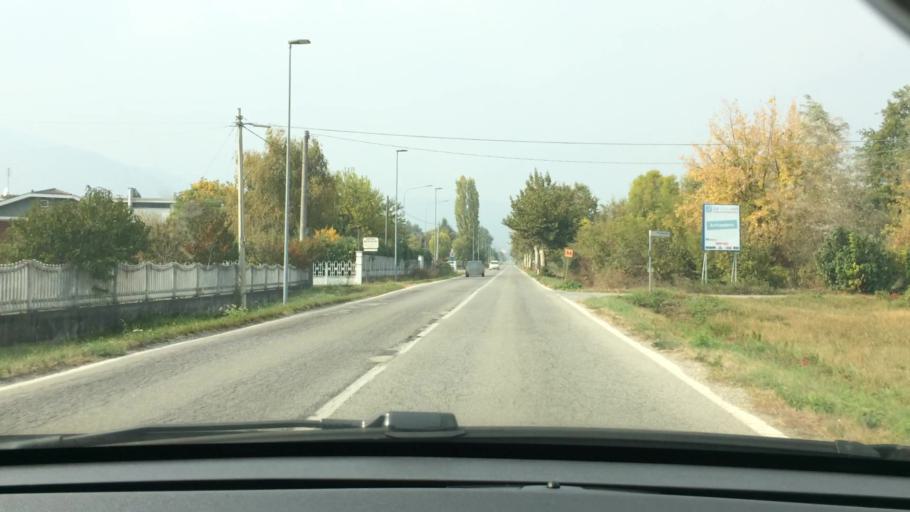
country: IT
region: Piedmont
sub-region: Provincia di Torino
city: Cumiana
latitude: 44.9608
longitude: 7.4023
